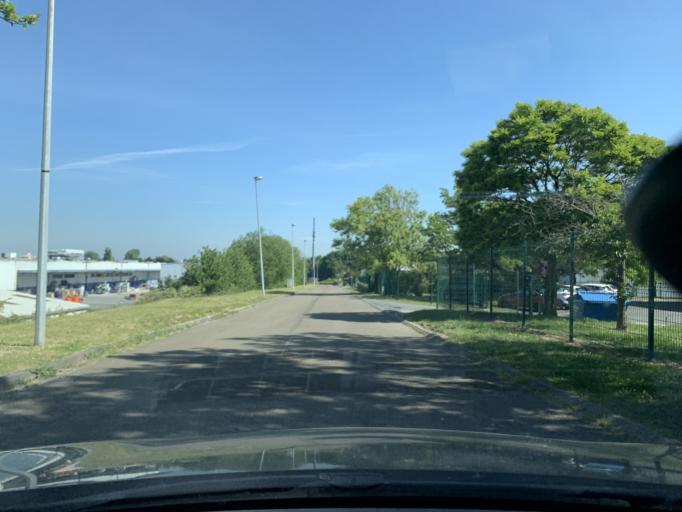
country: FR
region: Nord-Pas-de-Calais
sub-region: Departement du Nord
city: Rumilly-en-Cambresis
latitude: 50.1462
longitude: 3.2241
